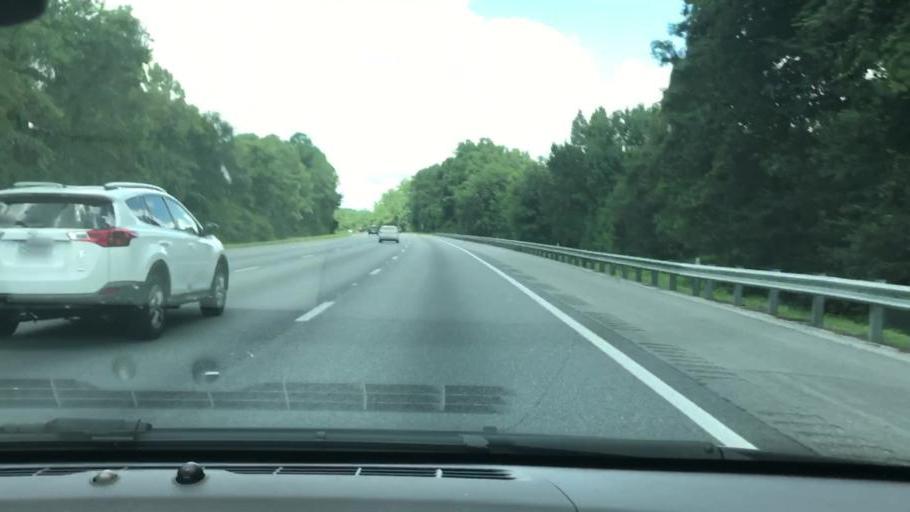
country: US
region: Florida
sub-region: Alachua County
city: Alachua
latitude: 29.7389
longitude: -82.4773
